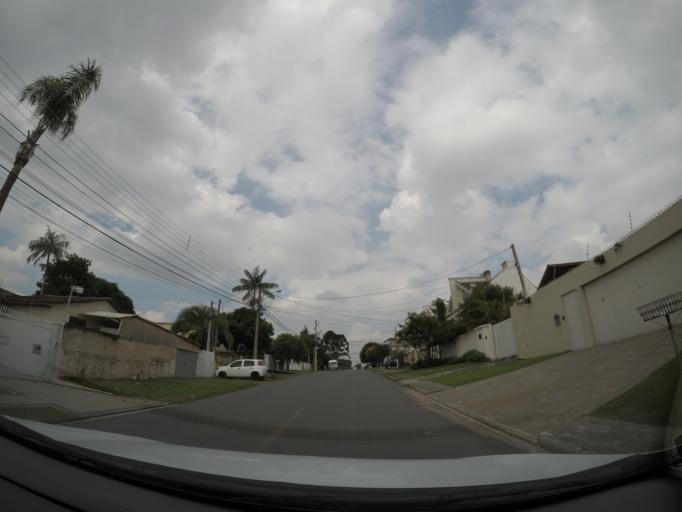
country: BR
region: Parana
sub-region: Sao Jose Dos Pinhais
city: Sao Jose dos Pinhais
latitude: -25.4957
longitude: -49.2486
